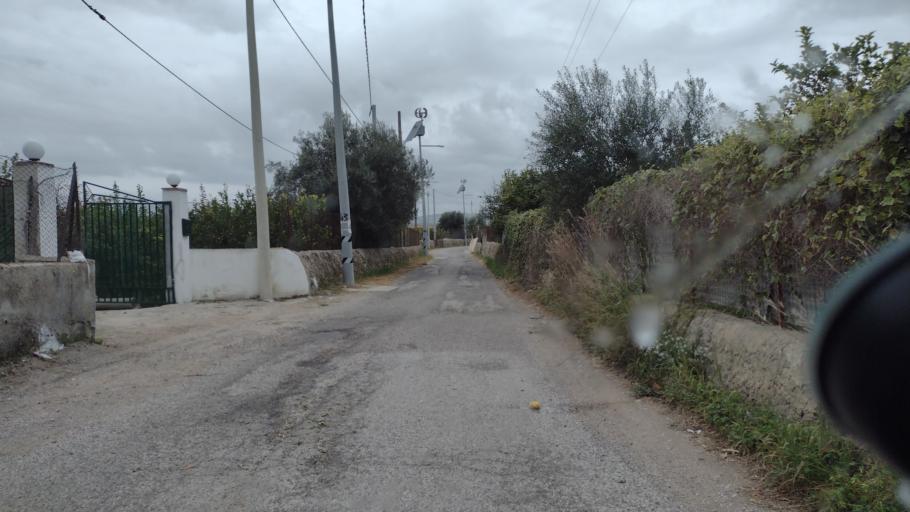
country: IT
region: Sicily
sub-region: Provincia di Siracusa
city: Avola
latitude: 36.8865
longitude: 15.1225
